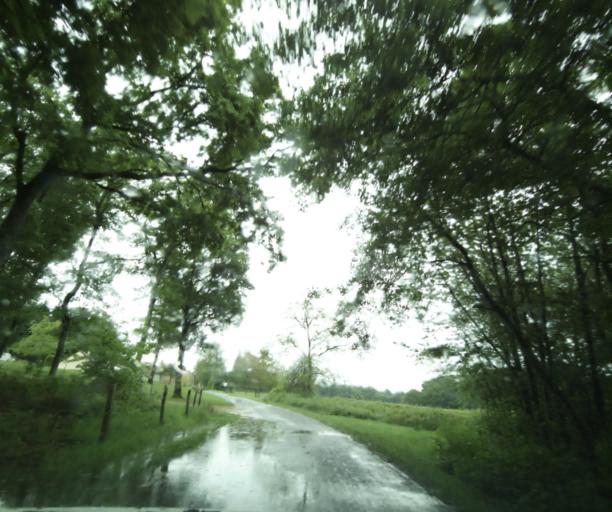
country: FR
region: Bourgogne
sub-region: Departement de Saone-et-Loire
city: Ciry-le-Noble
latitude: 46.5426
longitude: 4.3041
